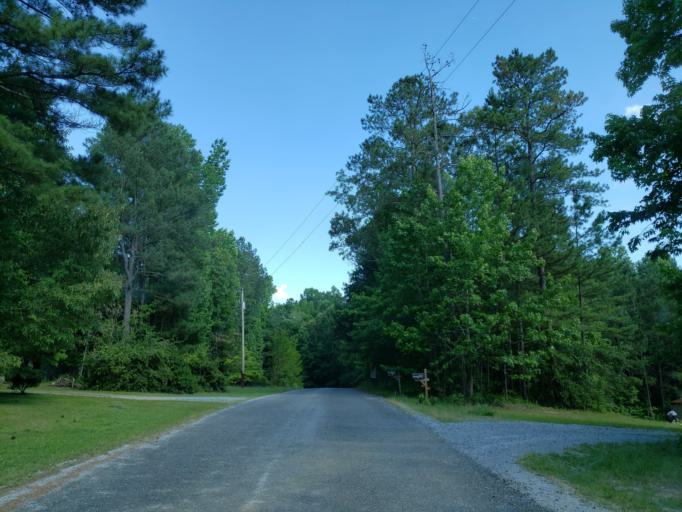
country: US
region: Georgia
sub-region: Carroll County
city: Temple
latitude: 33.8169
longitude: -85.0892
